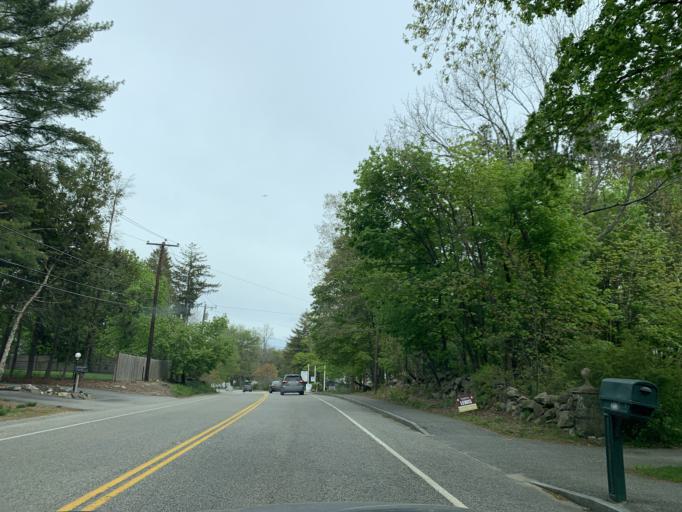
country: US
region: Massachusetts
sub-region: Norfolk County
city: Sharon
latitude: 42.1364
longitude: -71.1638
